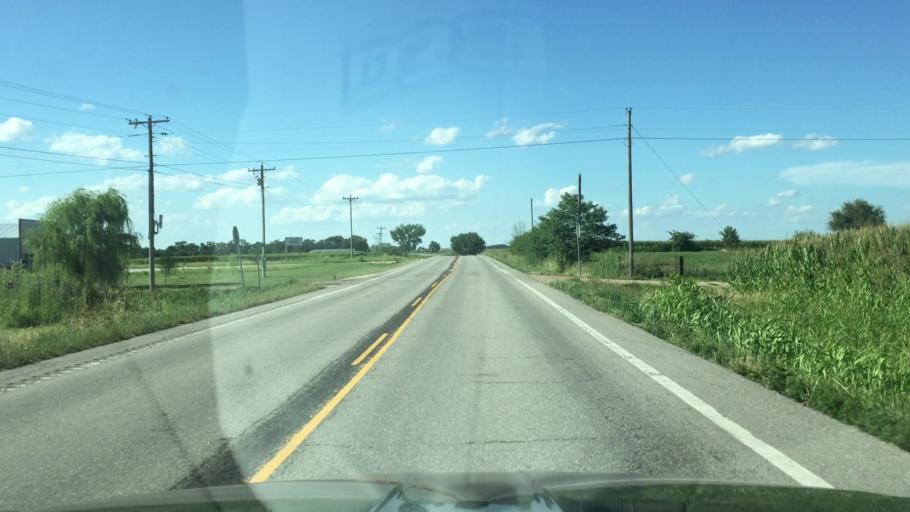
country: US
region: Missouri
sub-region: Moniteau County
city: Tipton
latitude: 38.5884
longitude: -92.7893
